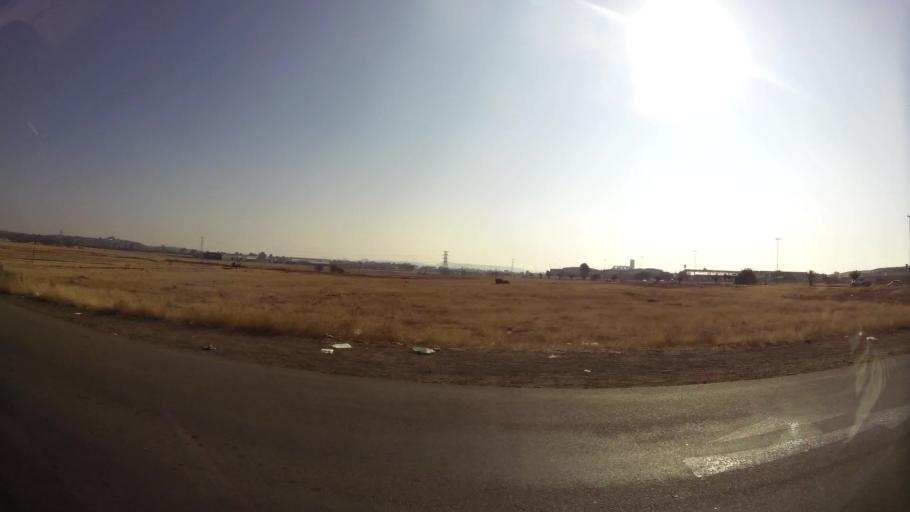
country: ZA
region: Orange Free State
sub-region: Mangaung Metropolitan Municipality
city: Bloemfontein
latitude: -29.1724
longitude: 26.2197
